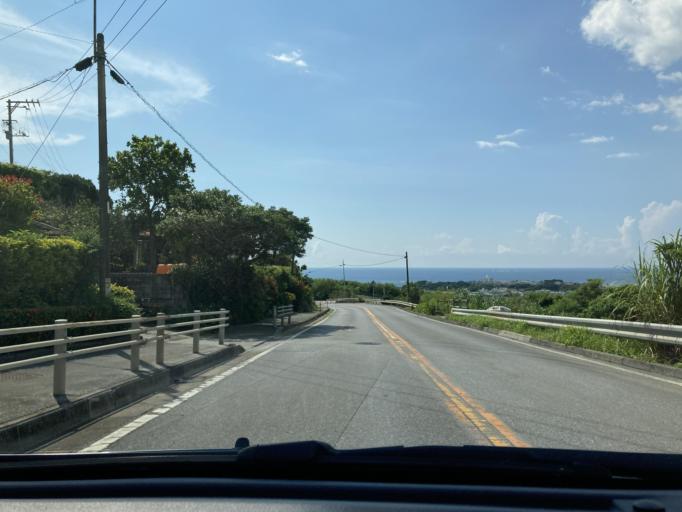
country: JP
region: Okinawa
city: Tomigusuku
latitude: 26.1408
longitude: 127.7719
